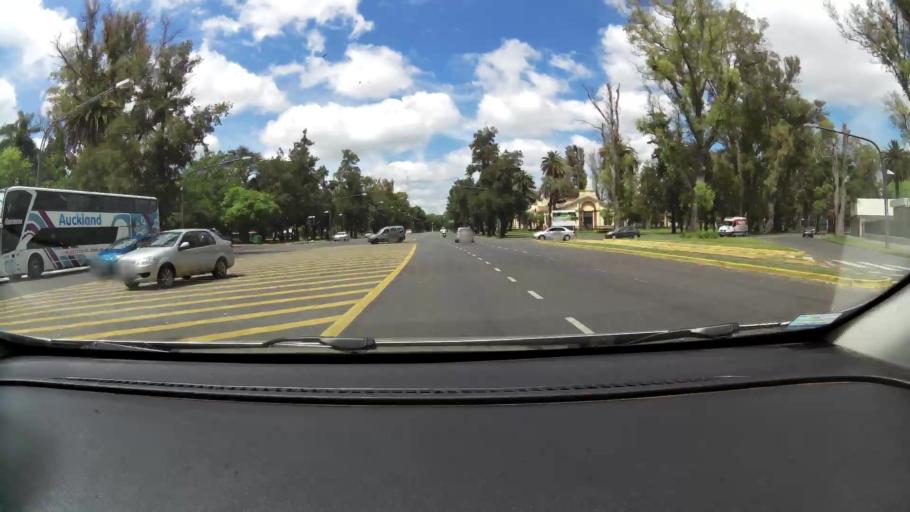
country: AR
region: Santa Fe
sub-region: Departamento de Rosario
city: Rosario
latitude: -32.9622
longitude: -60.6580
